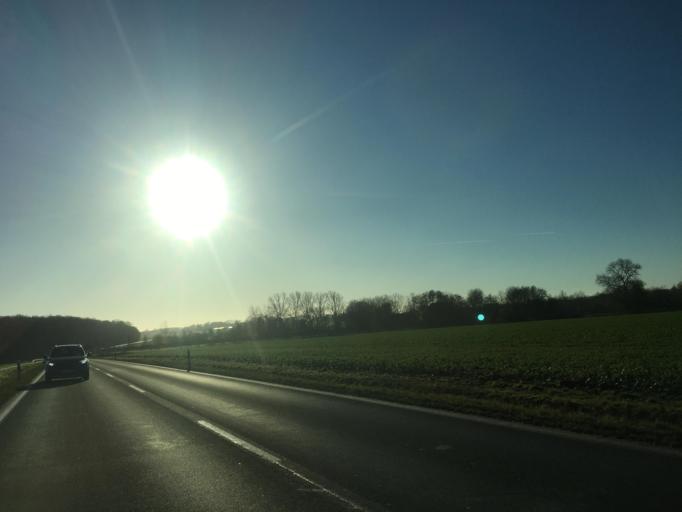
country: DE
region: North Rhine-Westphalia
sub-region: Regierungsbezirk Munster
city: Dulmen
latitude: 51.8780
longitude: 7.2890
